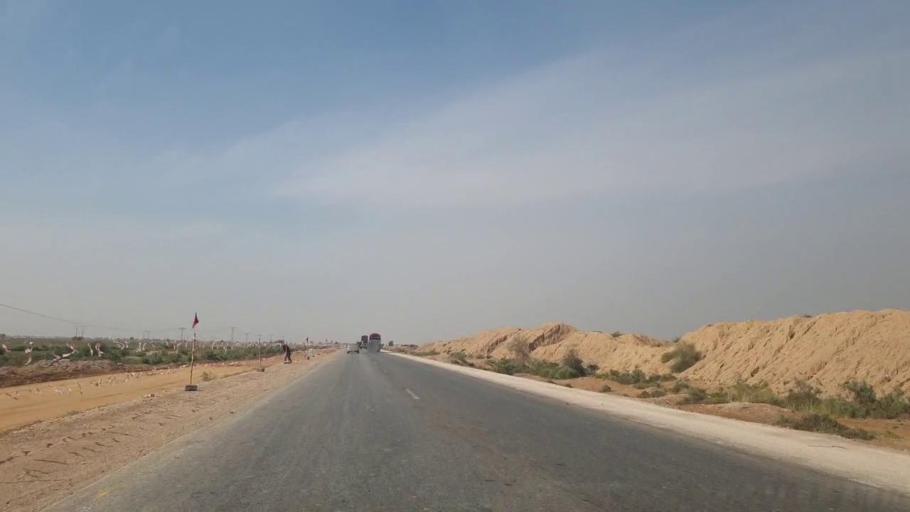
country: PK
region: Sindh
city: Sann
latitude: 26.0136
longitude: 68.1449
